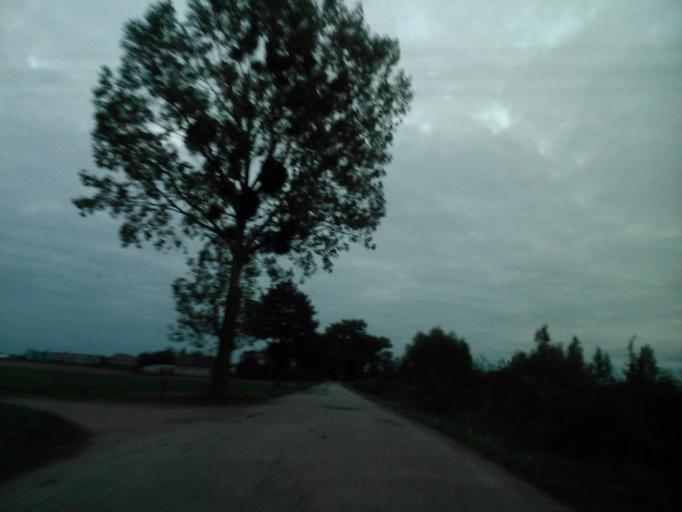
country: PL
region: Kujawsko-Pomorskie
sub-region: Powiat golubsko-dobrzynski
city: Kowalewo Pomorskie
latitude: 53.1085
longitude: 18.8719
